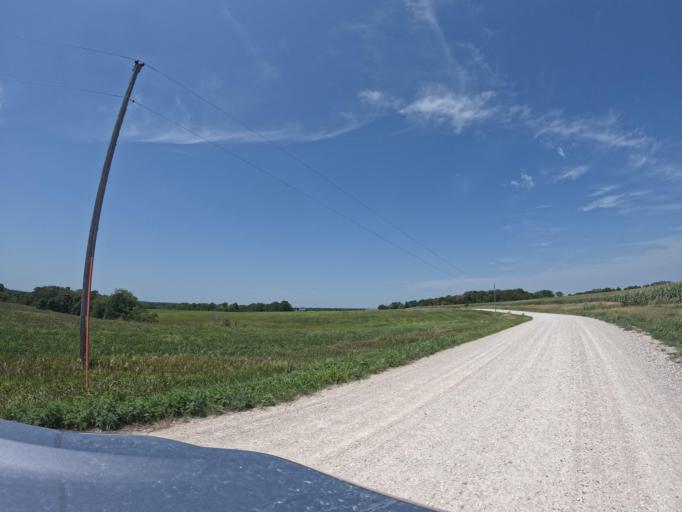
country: US
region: Iowa
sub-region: Henry County
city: Mount Pleasant
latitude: 40.9106
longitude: -91.6549
